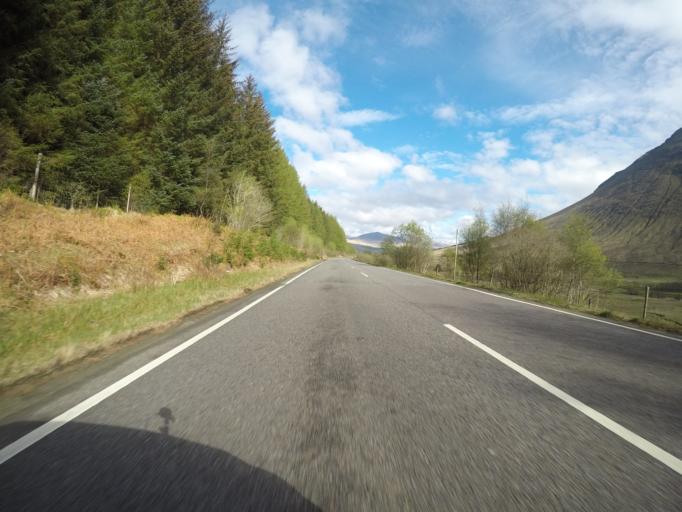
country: GB
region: Scotland
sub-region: Argyll and Bute
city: Garelochhead
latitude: 56.4832
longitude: -4.7381
